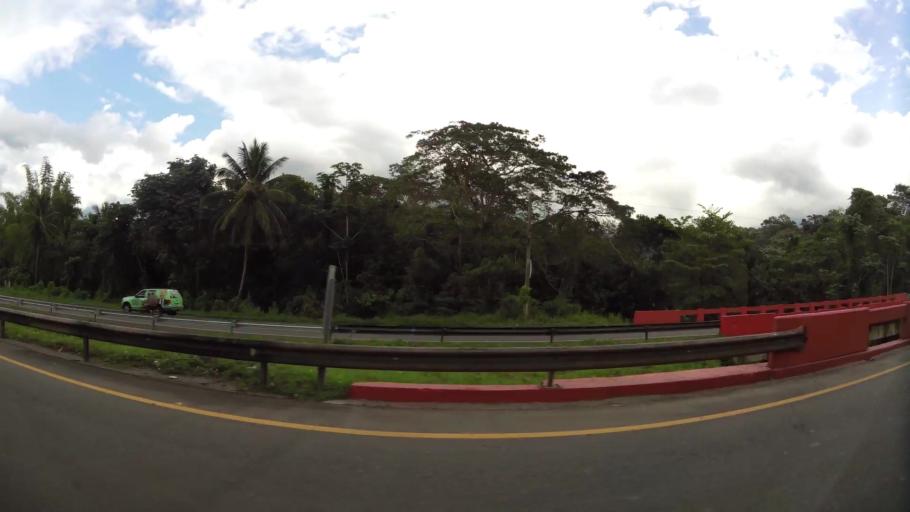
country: DO
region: Monsenor Nouel
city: Piedra Blanca
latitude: 18.8340
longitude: -70.2997
